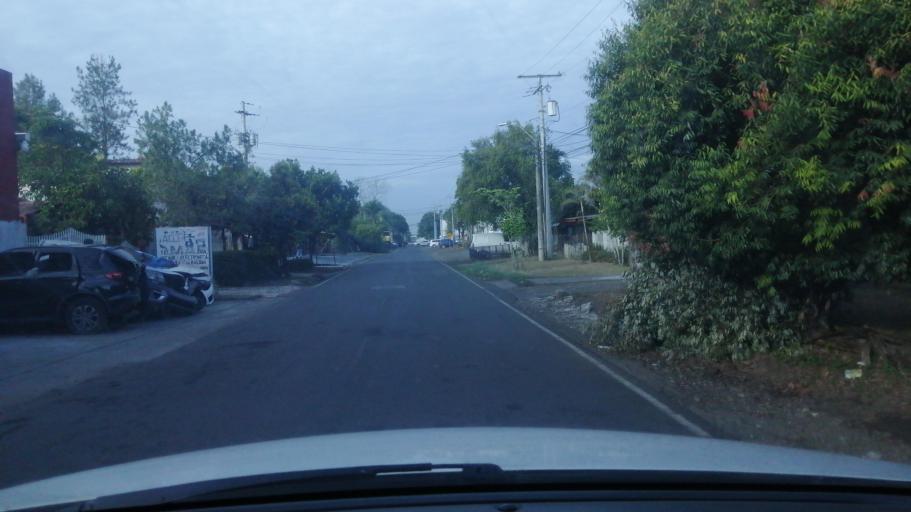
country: PA
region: Chiriqui
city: David
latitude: 8.4373
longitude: -82.4365
